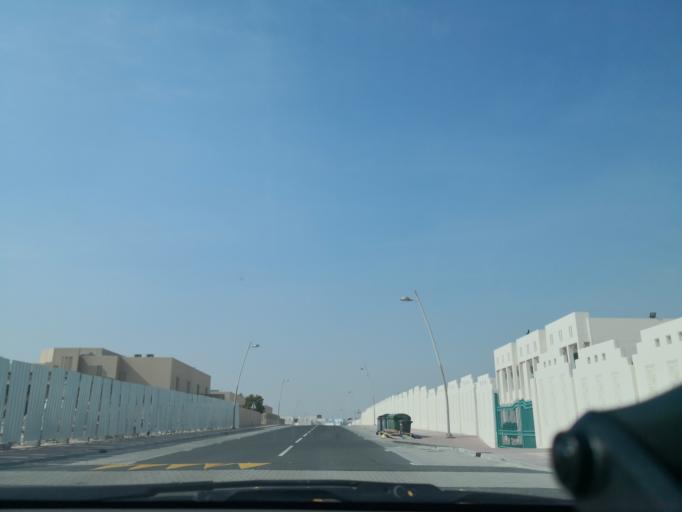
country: QA
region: Baladiyat ad Dawhah
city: Doha
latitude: 25.3445
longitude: 51.4972
